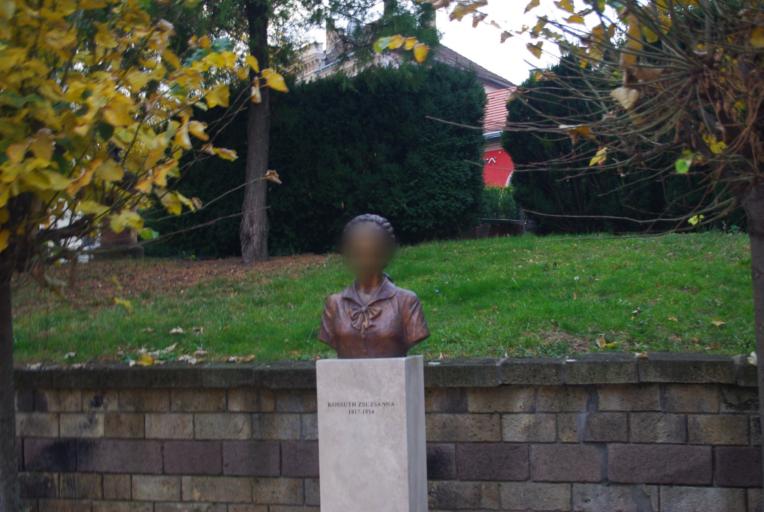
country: HU
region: Borsod-Abauj-Zemplen
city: Satoraljaujhely
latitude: 48.3951
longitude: 21.6559
